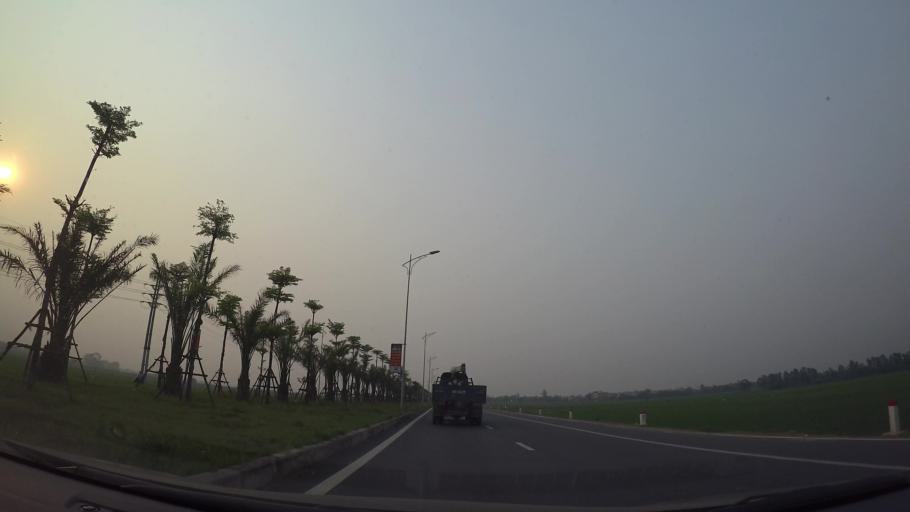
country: VN
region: Ha Noi
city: Kim Bai
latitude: 20.8870
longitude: 105.7968
